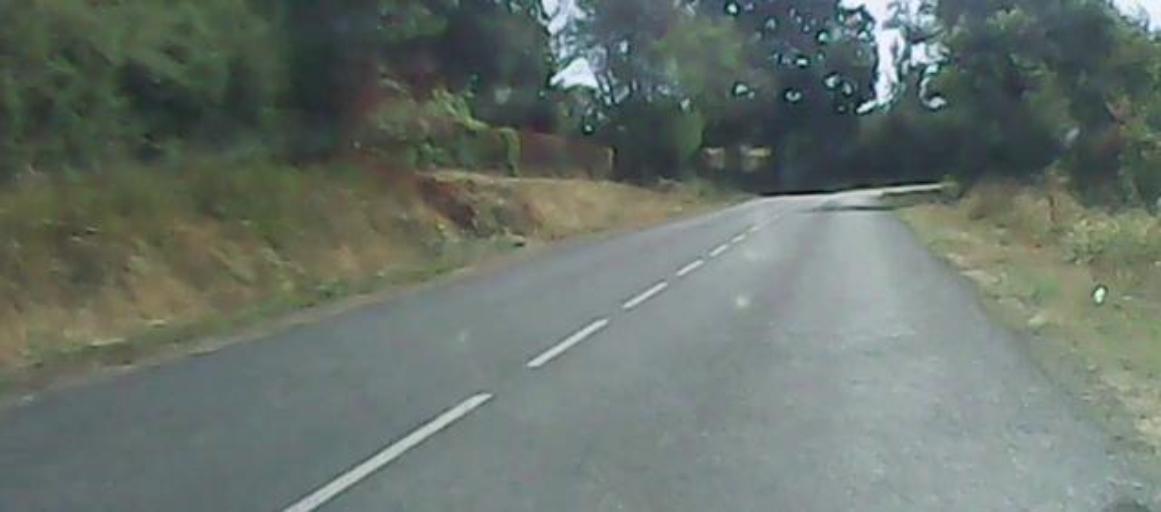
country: FR
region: Auvergne
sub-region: Departement de l'Allier
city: Saint-Yorre
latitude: 46.0652
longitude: 3.4840
